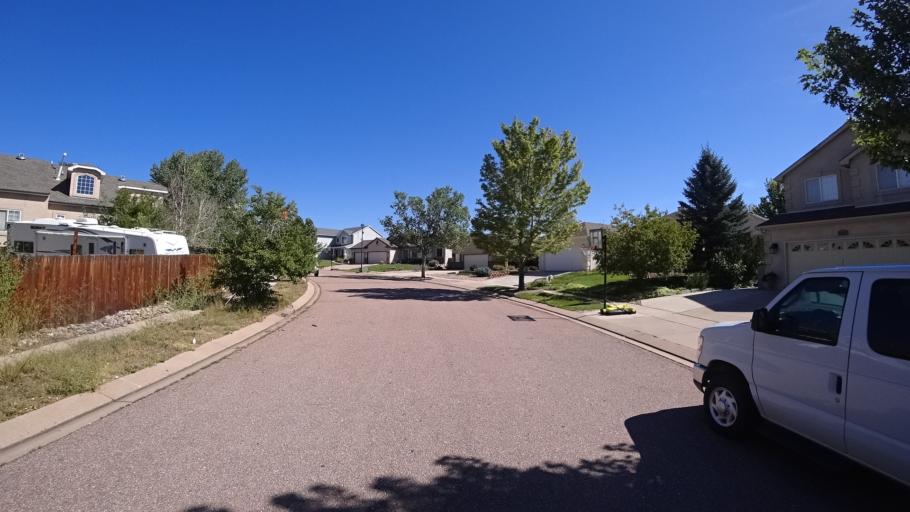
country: US
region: Colorado
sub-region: El Paso County
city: Black Forest
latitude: 38.9511
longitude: -104.7252
